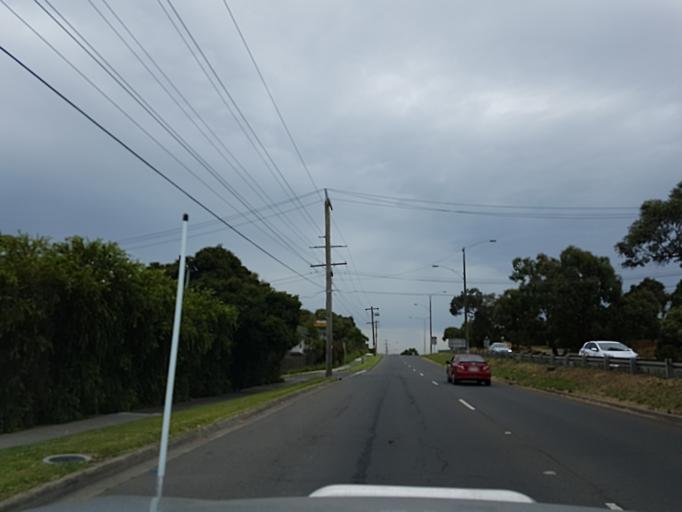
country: AU
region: Victoria
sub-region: Knox
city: Bayswater
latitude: -37.8600
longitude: 145.2652
